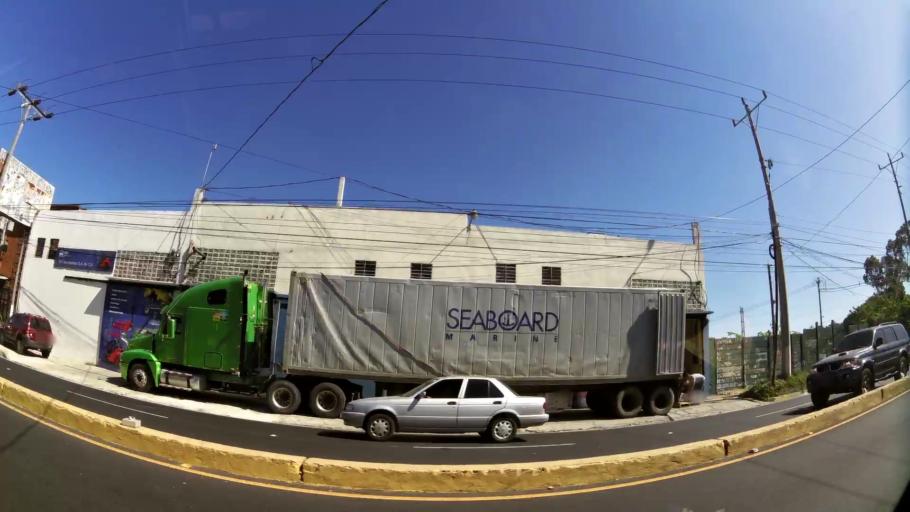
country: SV
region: La Libertad
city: Santa Tecla
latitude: 13.6646
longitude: -89.2800
